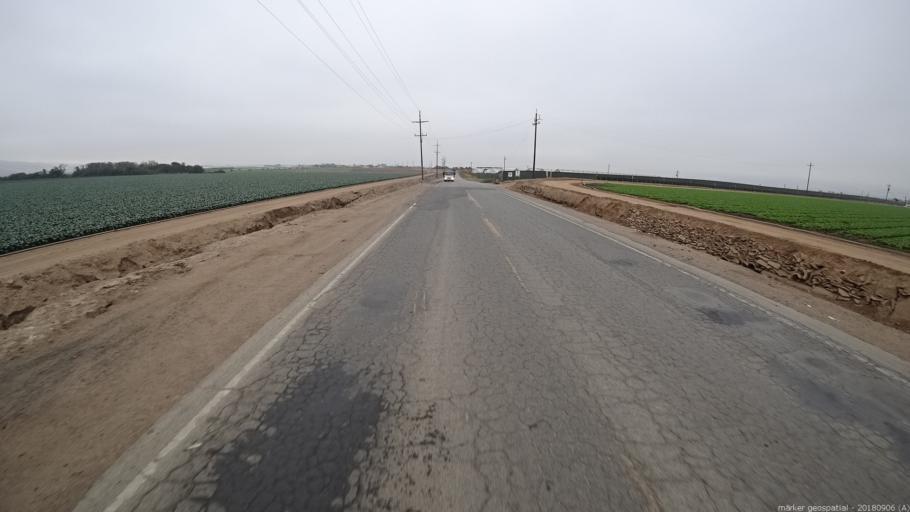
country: US
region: California
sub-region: Monterey County
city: Salinas
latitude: 36.6480
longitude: -121.5792
